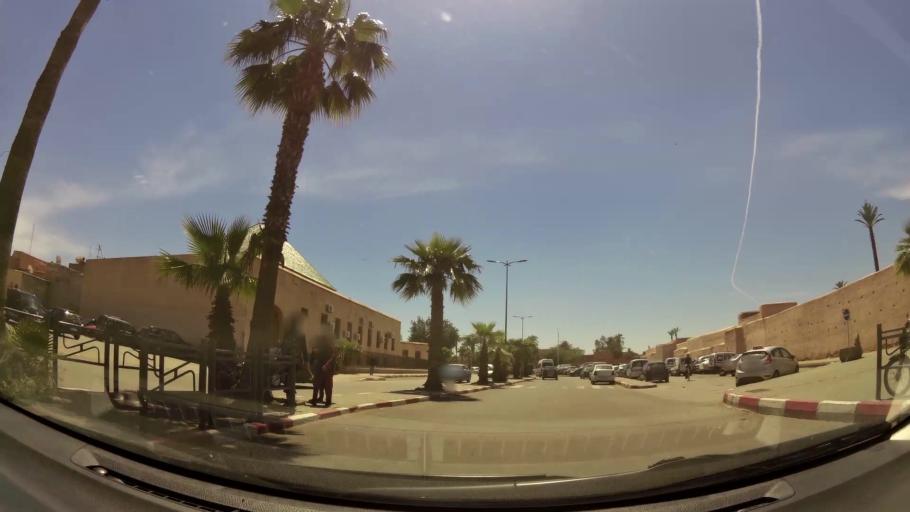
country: MA
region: Marrakech-Tensift-Al Haouz
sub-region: Marrakech
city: Marrakesh
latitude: 31.6331
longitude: -7.9993
